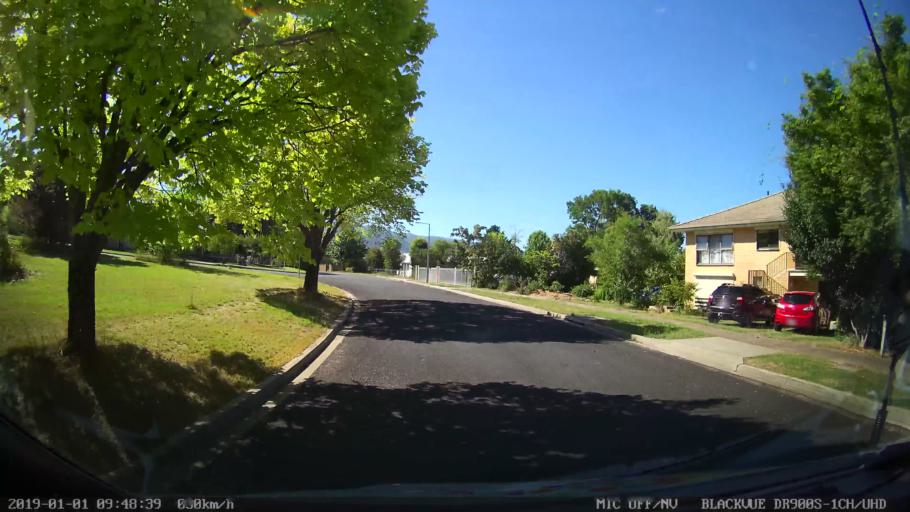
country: AU
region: New South Wales
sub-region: Snowy River
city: Jindabyne
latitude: -36.2125
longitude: 148.1320
